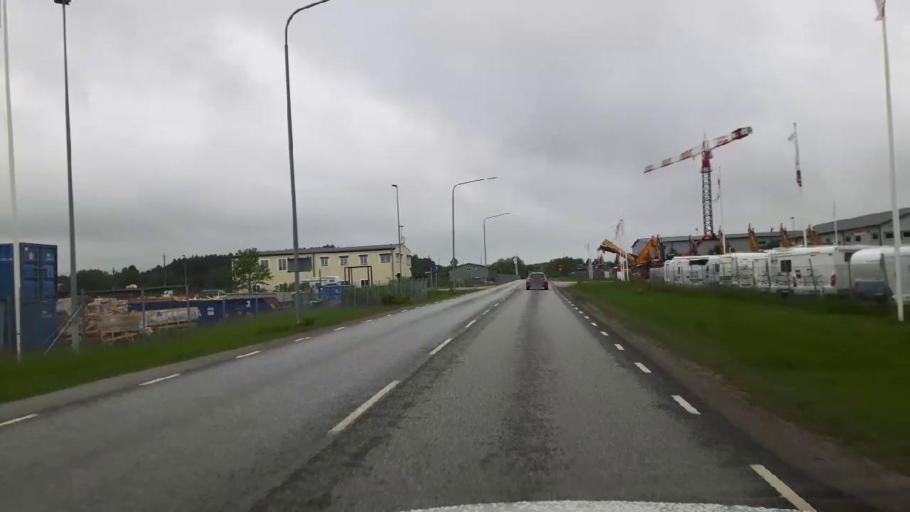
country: SE
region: Stockholm
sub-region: Upplands-Bro Kommun
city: Bro
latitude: 59.5158
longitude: 17.6251
